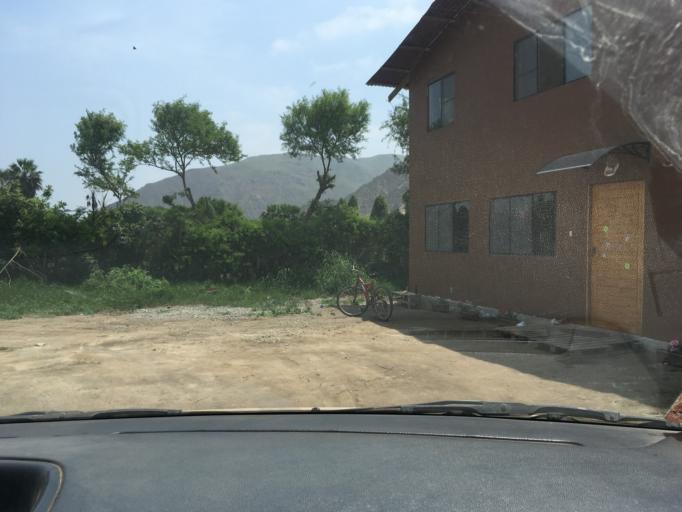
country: PE
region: Lima
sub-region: Lima
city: Cieneguilla
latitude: -12.1911
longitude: -76.8646
